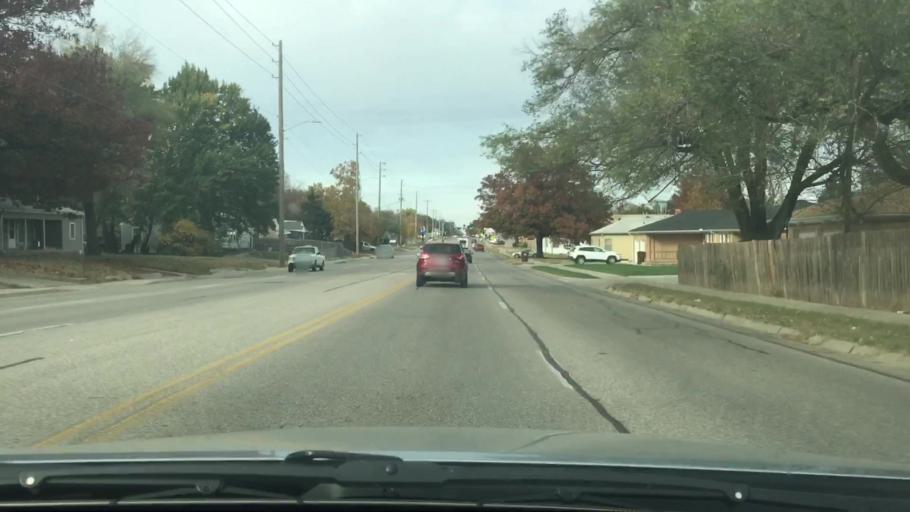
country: US
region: Kansas
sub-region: Sedgwick County
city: Wichita
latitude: 37.6740
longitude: -97.2804
